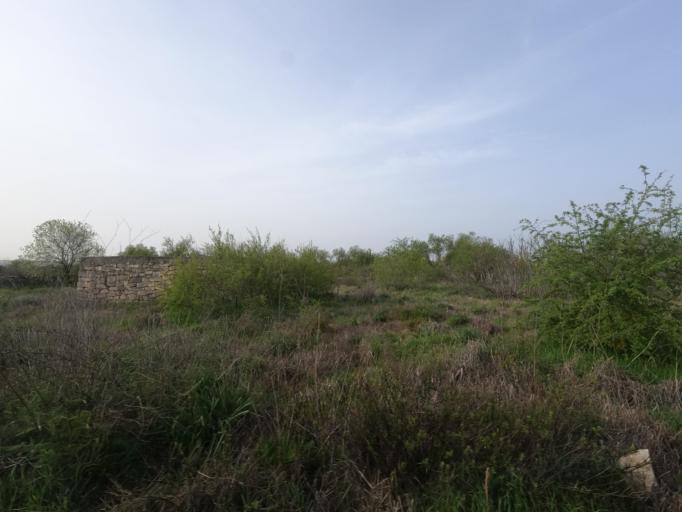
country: CY
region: Pafos
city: Pegeia
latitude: 34.9570
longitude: 32.3990
